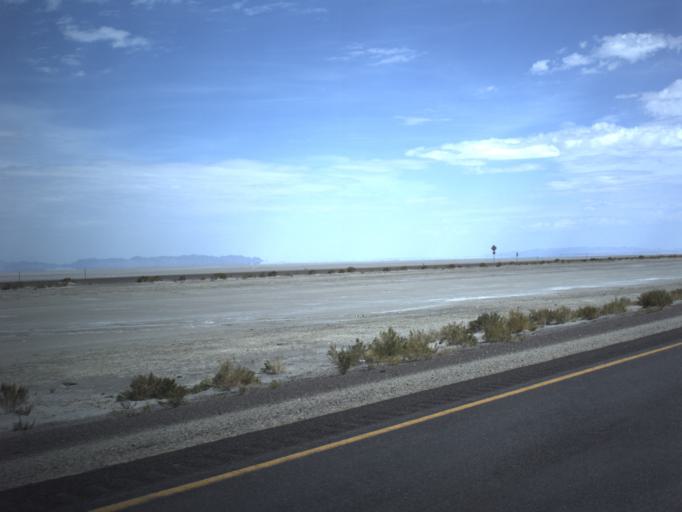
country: US
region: Utah
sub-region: Tooele County
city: Wendover
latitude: 40.7367
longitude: -113.7630
